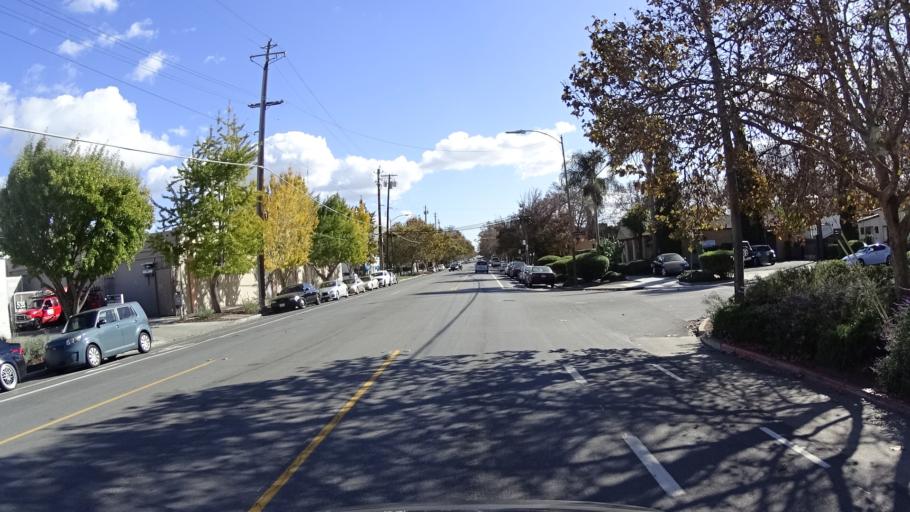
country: US
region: California
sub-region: Santa Clara County
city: San Jose
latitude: 37.3385
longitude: -121.9111
